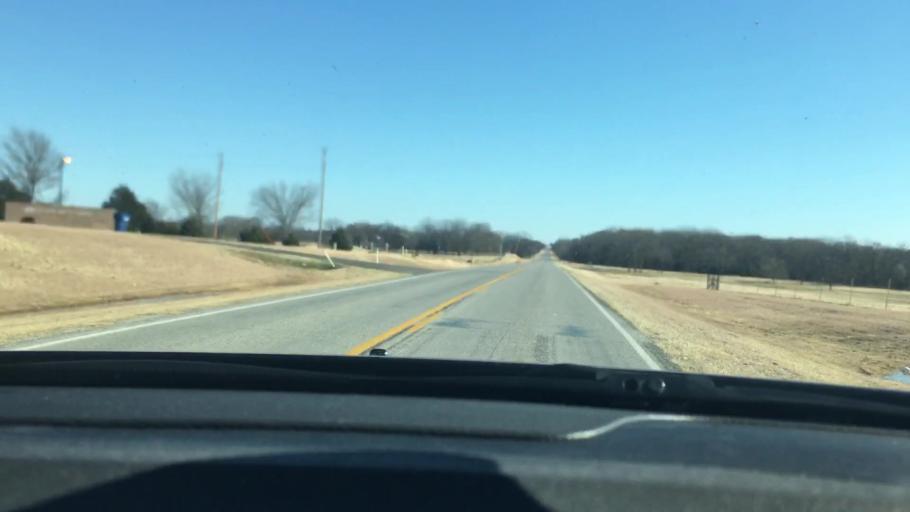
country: US
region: Oklahoma
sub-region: Garvin County
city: Wynnewood
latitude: 34.6516
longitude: -97.1354
